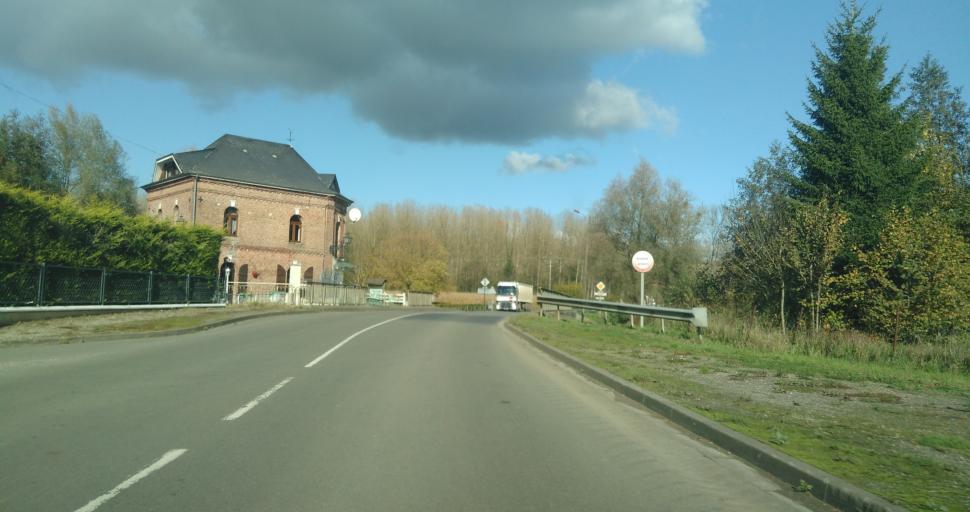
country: FR
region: Picardie
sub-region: Departement de la Somme
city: Doullens
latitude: 50.1633
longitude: 2.3002
